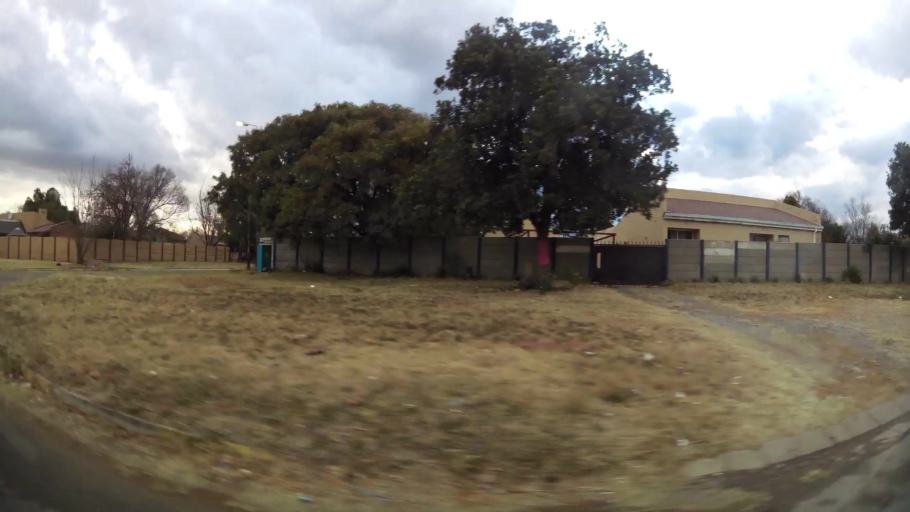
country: ZA
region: Orange Free State
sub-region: Lejweleputswa District Municipality
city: Welkom
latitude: -27.9512
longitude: 26.7349
